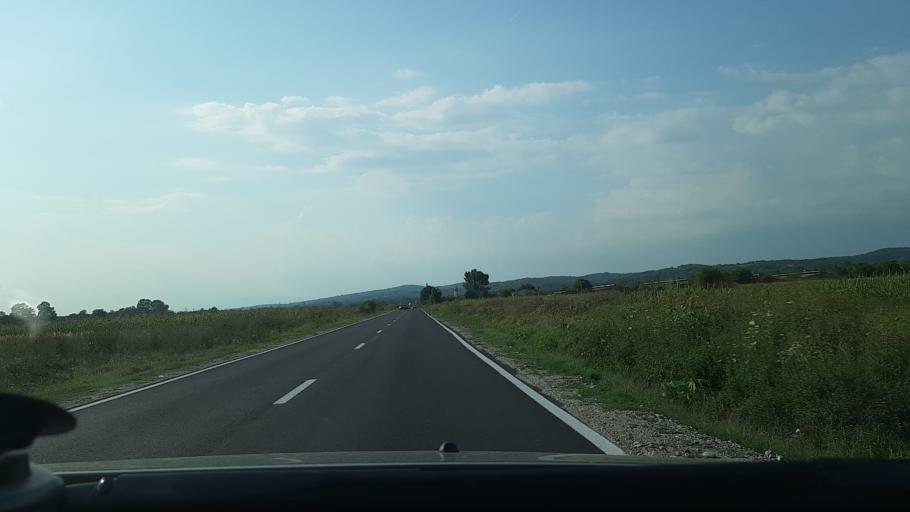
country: RO
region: Gorj
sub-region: Comuna Targu Carbunesti
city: Pojogeni
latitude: 45.0109
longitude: 23.4762
